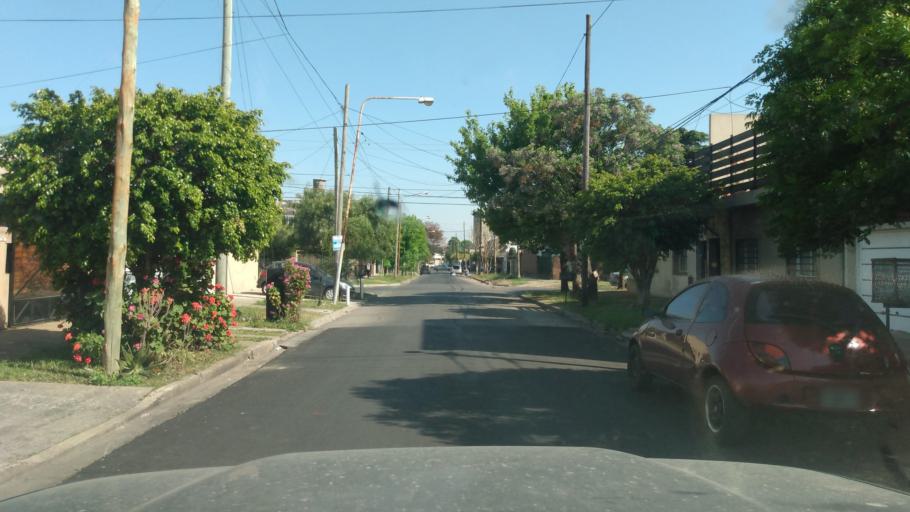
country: AR
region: Buenos Aires
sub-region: Partido de Moron
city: Moron
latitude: -34.6600
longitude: -58.5891
